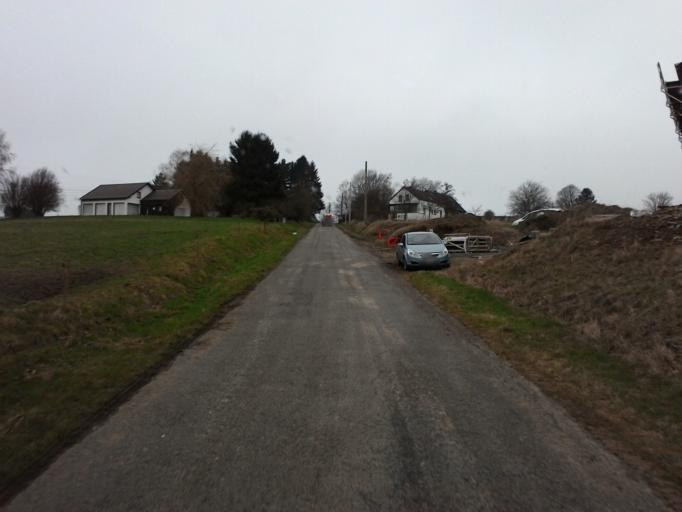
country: BE
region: Wallonia
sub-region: Province de Namur
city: Gedinne
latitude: 50.0233
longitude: 4.8626
